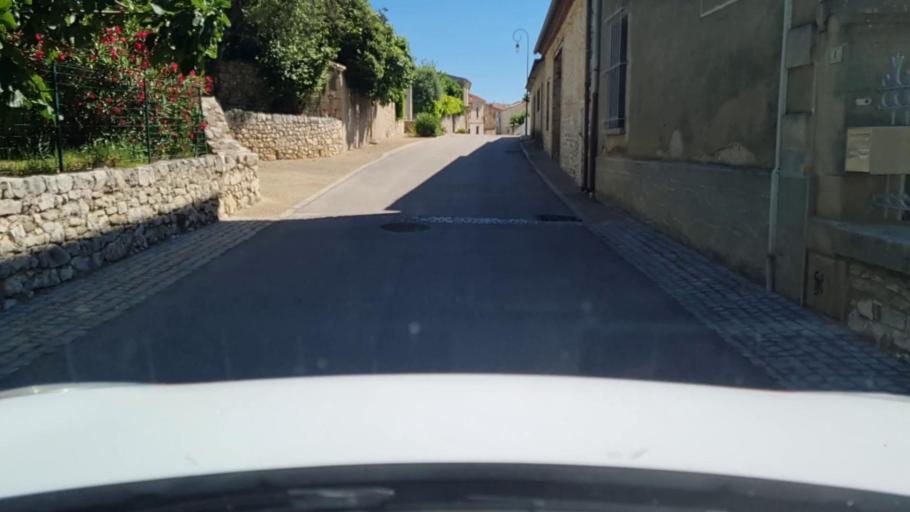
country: FR
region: Languedoc-Roussillon
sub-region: Departement du Gard
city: Villevieille
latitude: 43.8532
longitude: 4.1106
